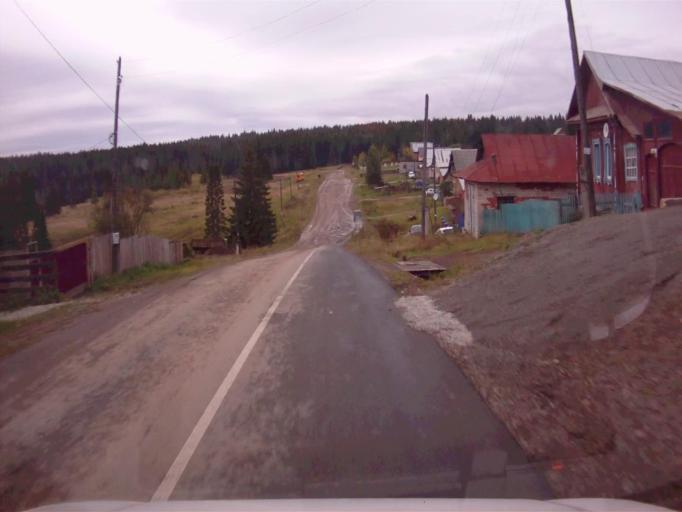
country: RU
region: Chelyabinsk
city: Nyazepetrovsk
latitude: 56.0632
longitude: 59.5725
